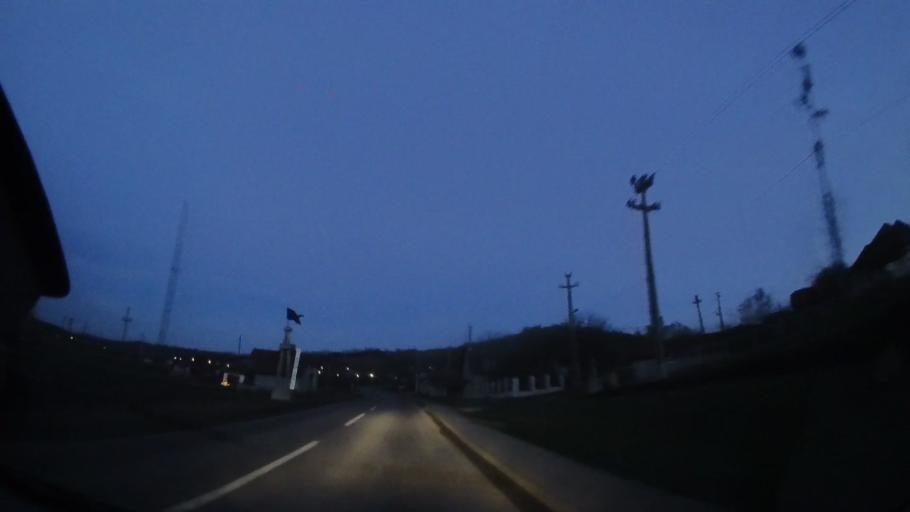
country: RO
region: Mures
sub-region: Comuna Sarmasu
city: Sarmasu
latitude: 46.7597
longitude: 24.1743
